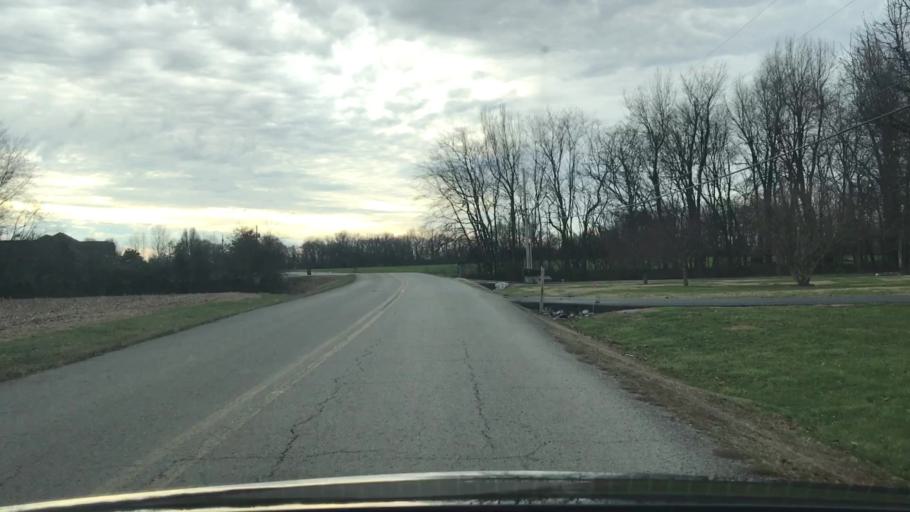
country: US
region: Kentucky
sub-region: Christian County
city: Hopkinsville
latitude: 36.8714
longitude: -87.5411
